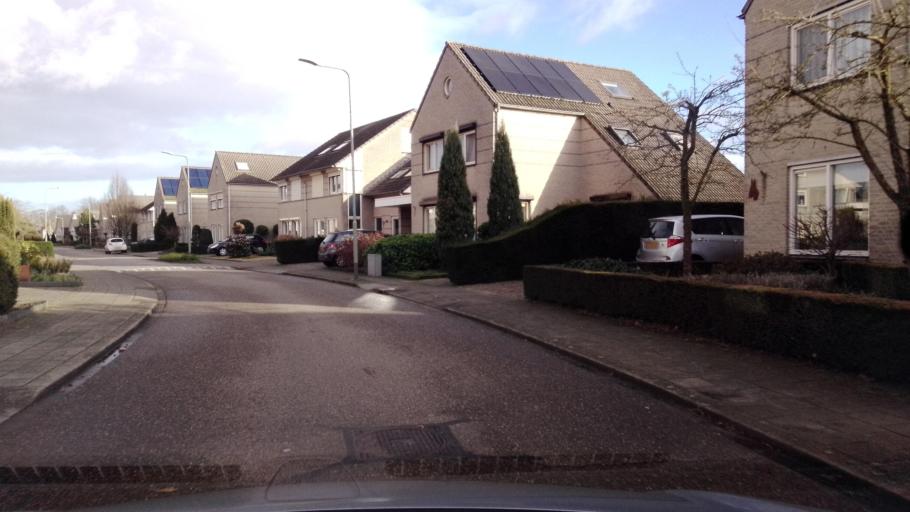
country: NL
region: Limburg
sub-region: Gemeente Peel en Maas
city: Maasbree
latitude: 51.4078
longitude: 6.0411
